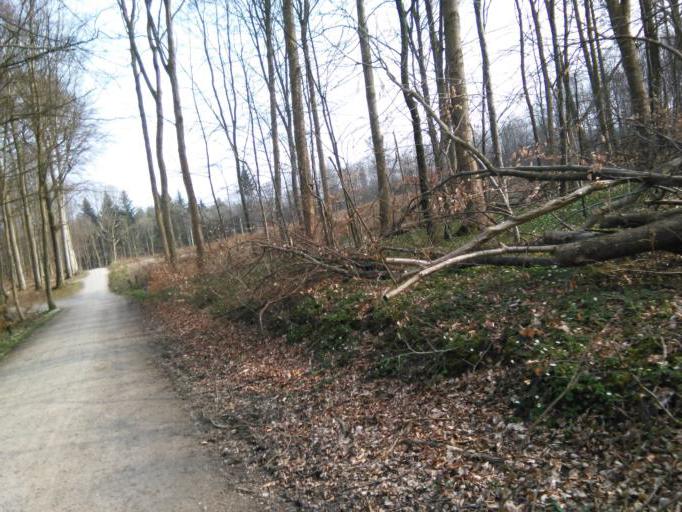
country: DK
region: Central Jutland
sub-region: Arhus Kommune
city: Beder
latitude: 56.0804
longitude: 10.2448
